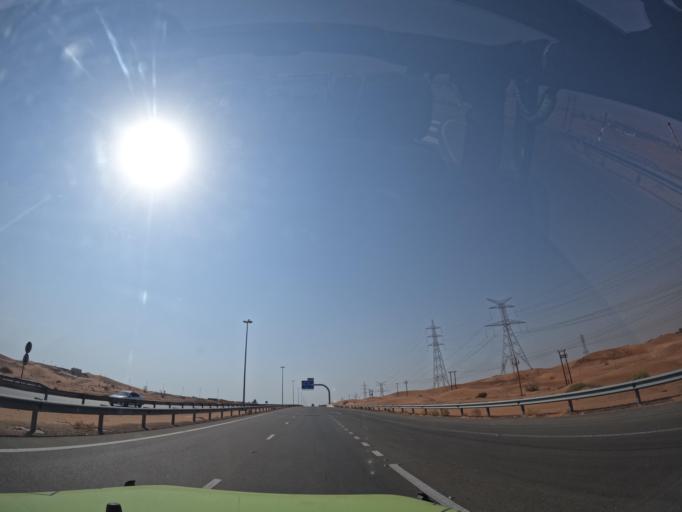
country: OM
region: Al Buraimi
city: Al Buraymi
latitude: 24.3498
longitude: 55.7373
